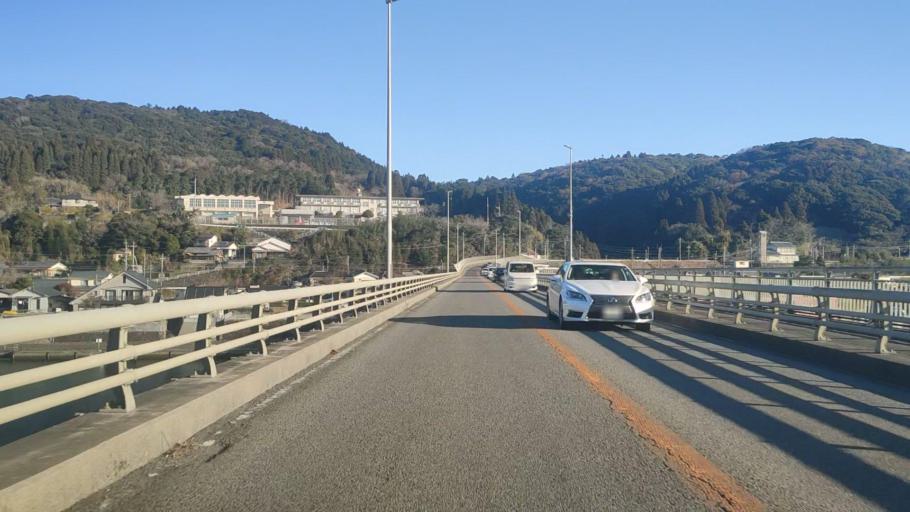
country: JP
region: Miyazaki
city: Takanabe
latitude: 32.3388
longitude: 131.6116
